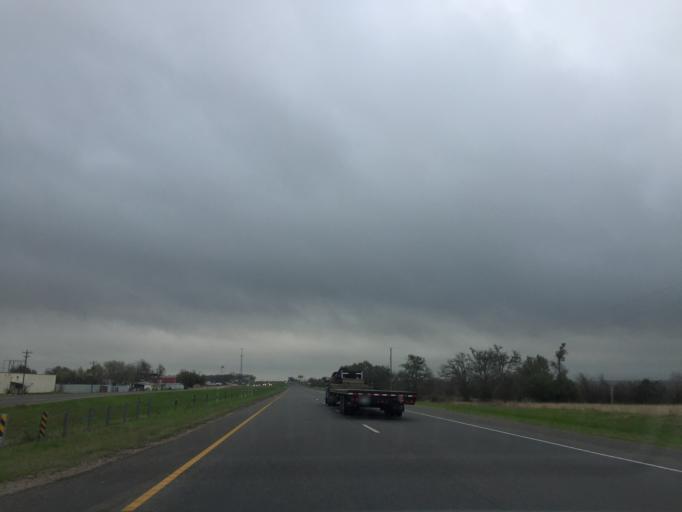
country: US
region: Texas
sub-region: Travis County
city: Garfield
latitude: 30.1888
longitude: -97.5701
